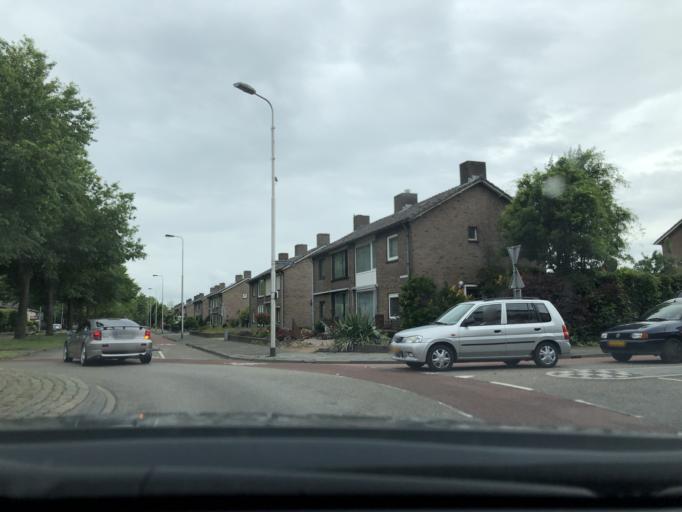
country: NL
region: North Brabant
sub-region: Gemeente Oss
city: Oss
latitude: 51.7728
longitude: 5.5257
